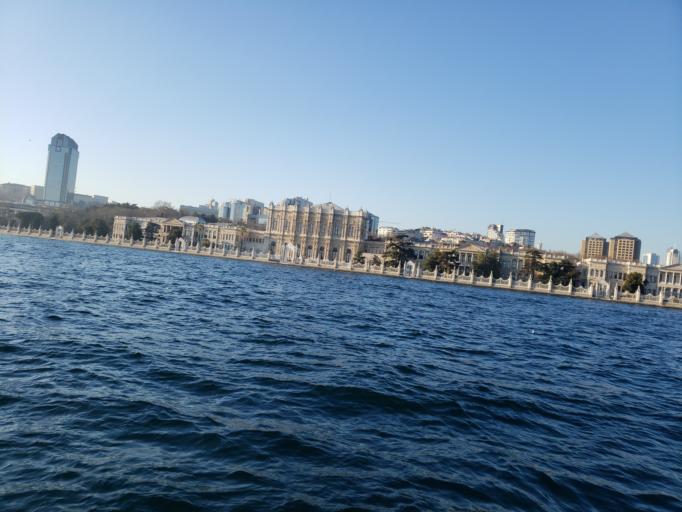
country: TR
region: Istanbul
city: UEskuedar
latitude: 41.0368
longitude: 29.0032
